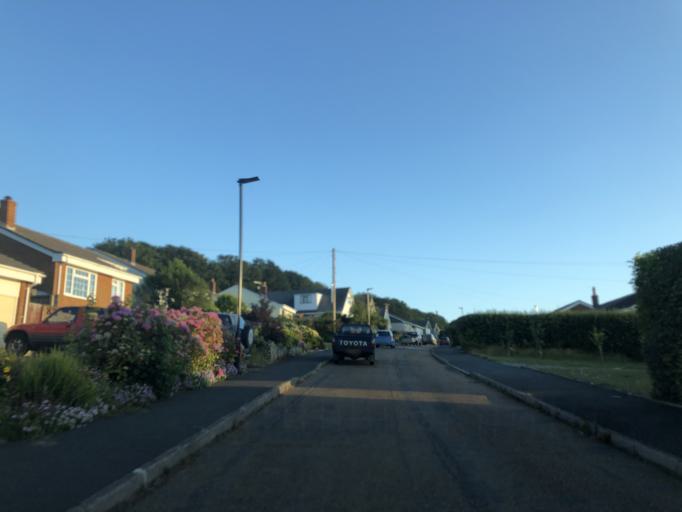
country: GB
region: England
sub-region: Isle of Wight
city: Niton
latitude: 50.5855
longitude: -1.2834
